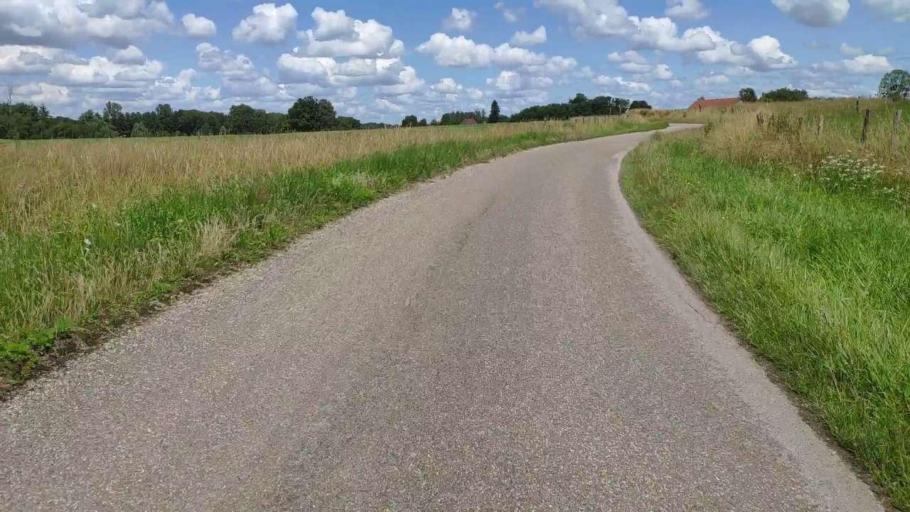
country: FR
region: Franche-Comte
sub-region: Departement du Jura
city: Chaussin
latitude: 46.8765
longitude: 5.4765
